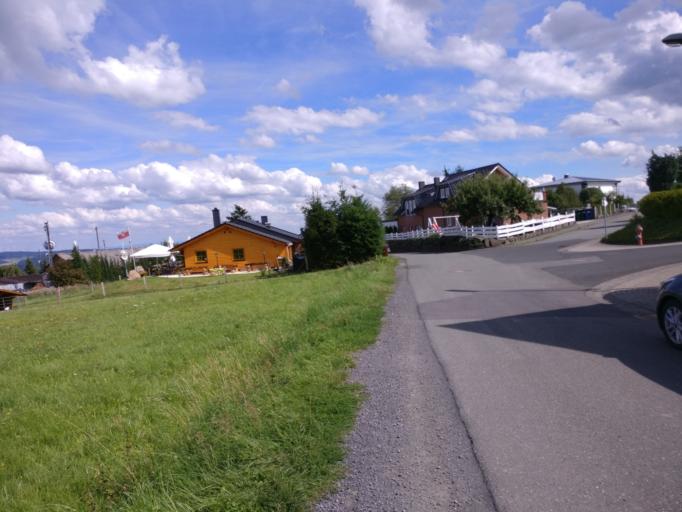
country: DE
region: Hesse
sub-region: Regierungsbezirk Giessen
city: Greifenstein
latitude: 50.6251
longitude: 8.2917
